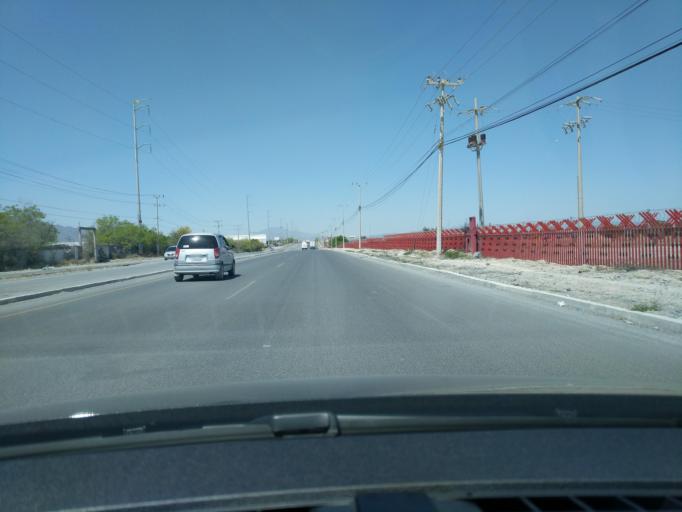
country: MX
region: Nuevo Leon
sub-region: Salinas Victoria
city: Emiliano Zapata
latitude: 25.8938
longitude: -100.2599
